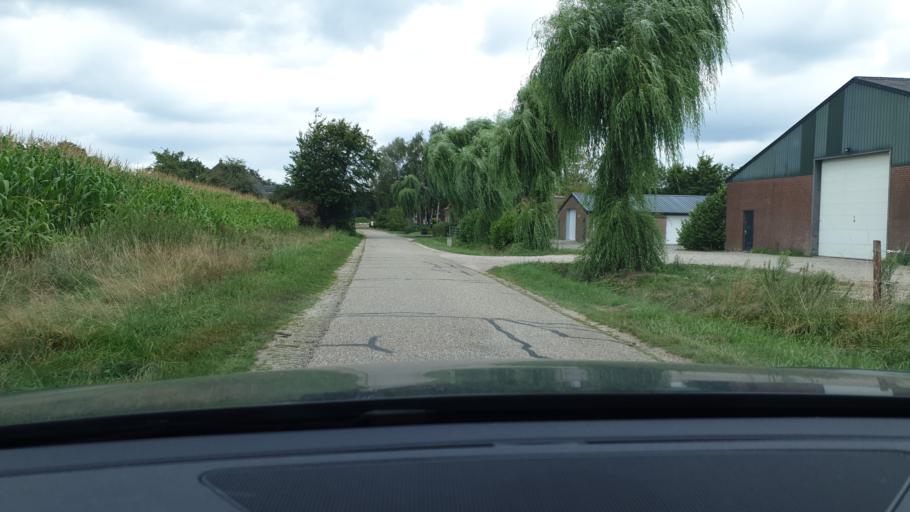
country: NL
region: North Brabant
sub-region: Gemeente Son en Breugel
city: Son
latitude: 51.5023
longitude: 5.4977
